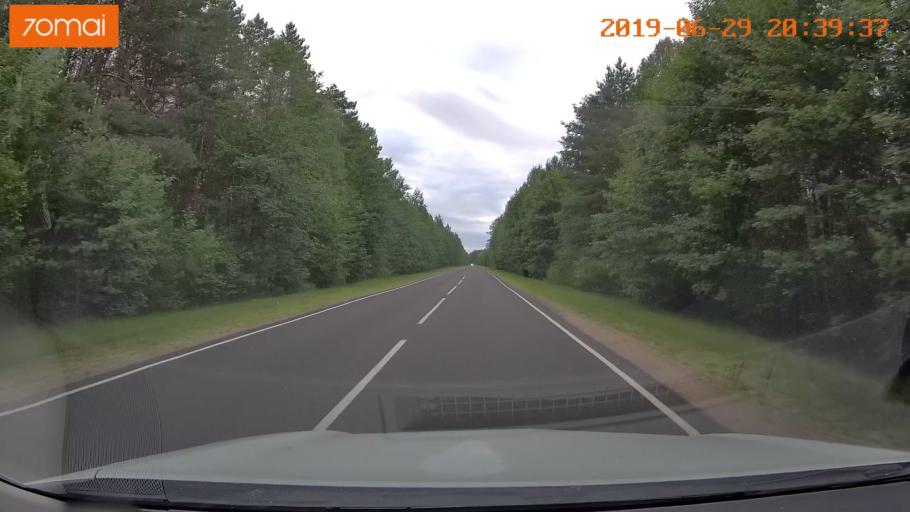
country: BY
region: Brest
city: Hantsavichy
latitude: 52.5647
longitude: 26.3612
